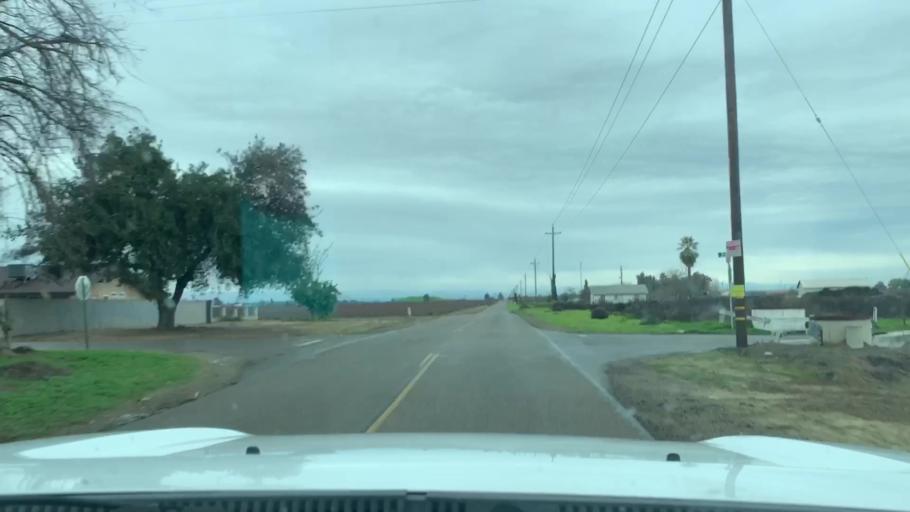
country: US
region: California
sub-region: Fresno County
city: Caruthers
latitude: 36.5474
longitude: -119.7732
